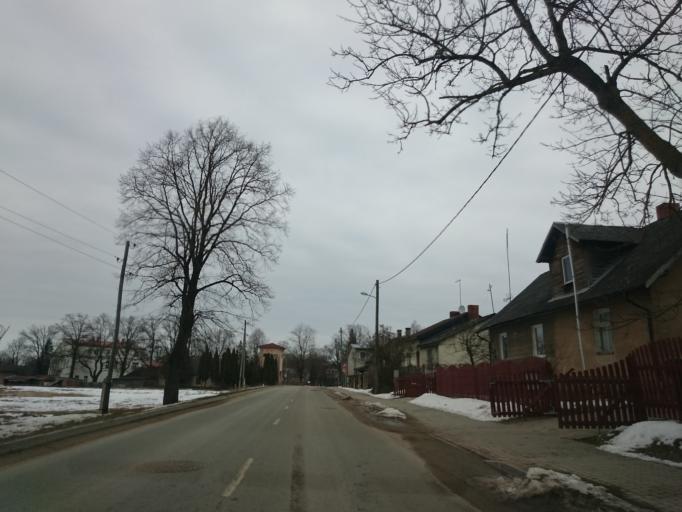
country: LV
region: Cesu Rajons
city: Cesis
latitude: 57.3071
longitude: 25.2607
